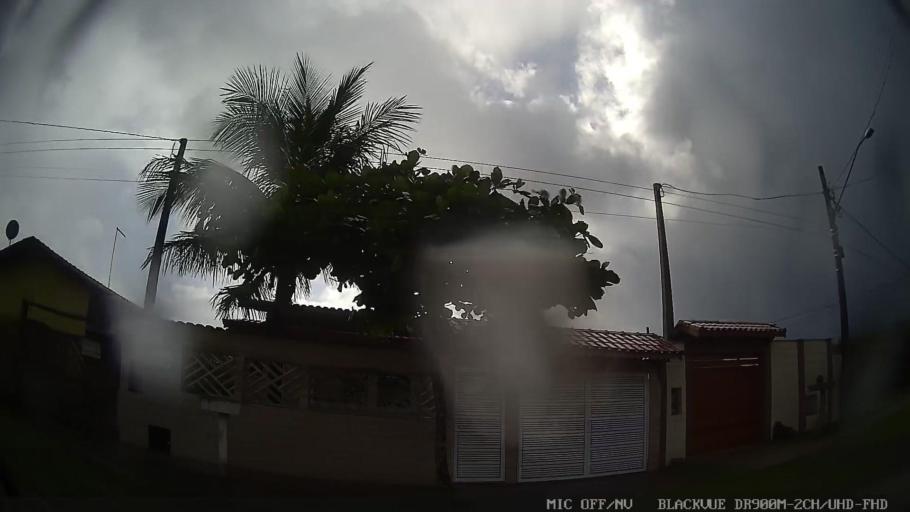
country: BR
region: Sao Paulo
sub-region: Itanhaem
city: Itanhaem
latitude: -24.2406
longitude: -46.9004
